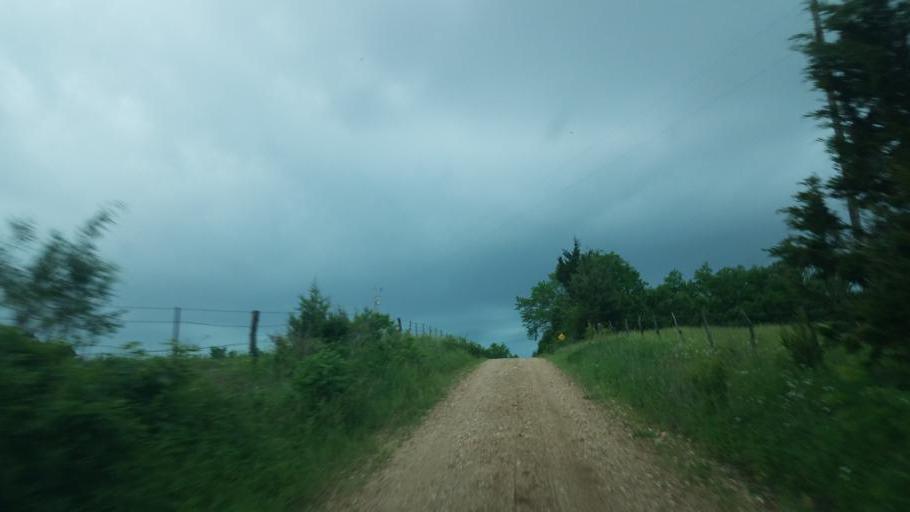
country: US
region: Missouri
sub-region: Moniteau County
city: California
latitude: 38.7503
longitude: -92.6250
